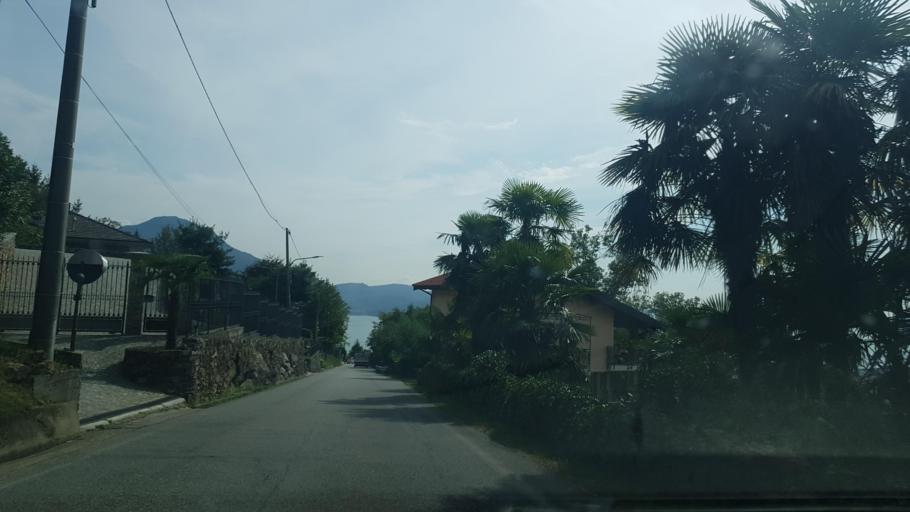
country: IT
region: Piedmont
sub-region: Provincia Verbano-Cusio-Ossola
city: Vignone
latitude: 45.9507
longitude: 8.5668
